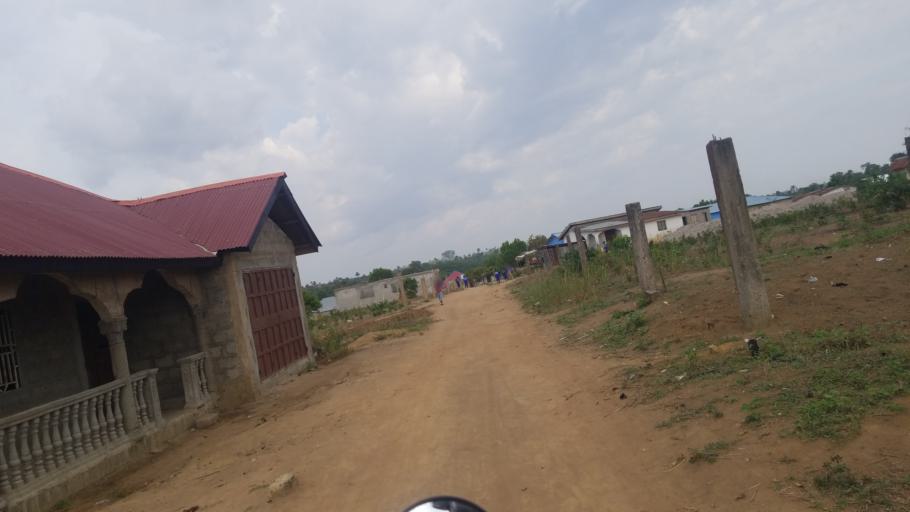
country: SL
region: Western Area
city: Waterloo
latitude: 8.3164
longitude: -13.0445
